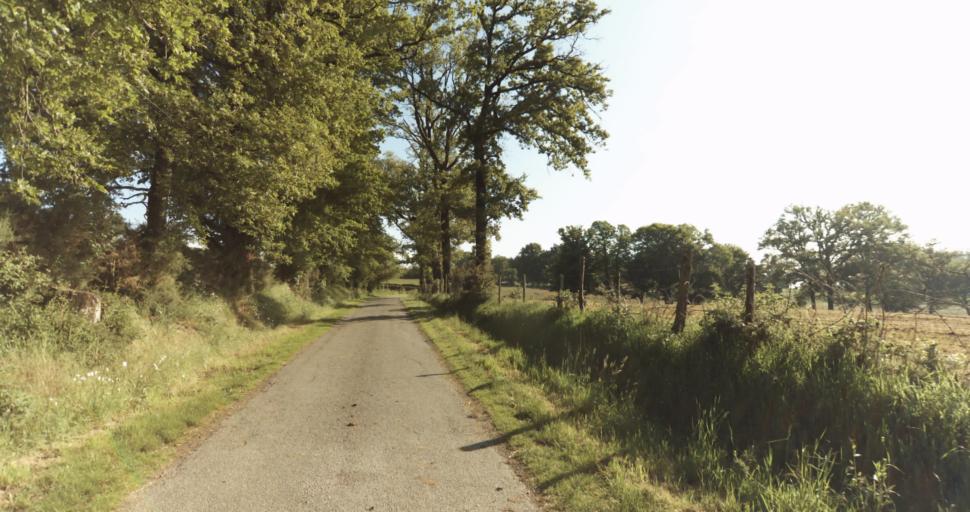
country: FR
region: Limousin
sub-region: Departement de la Haute-Vienne
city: Solignac
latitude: 45.7343
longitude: 1.2604
